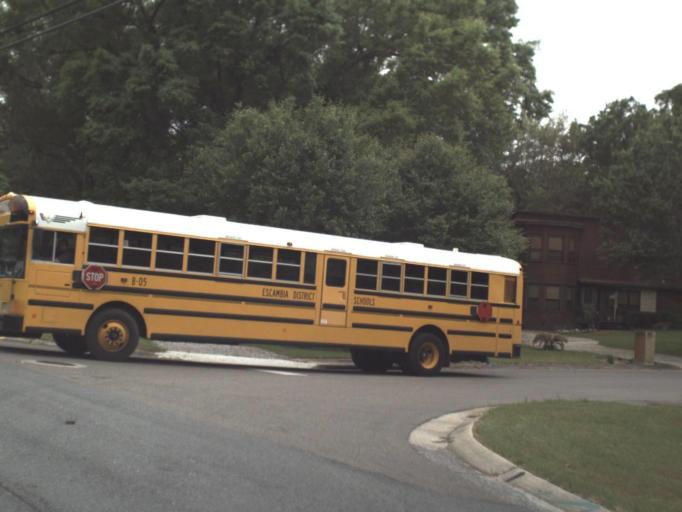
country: US
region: Florida
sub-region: Escambia County
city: Ferry Pass
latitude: 30.4971
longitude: -87.1601
